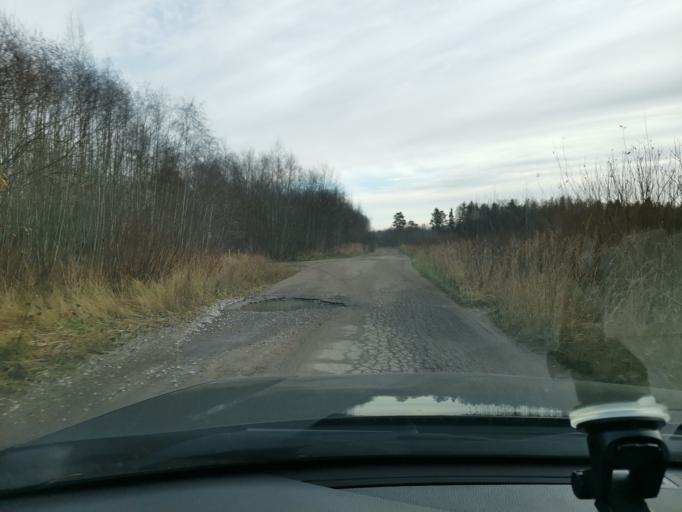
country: EE
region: Ida-Virumaa
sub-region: Sillamaee linn
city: Sillamae
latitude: 59.2595
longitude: 27.9114
